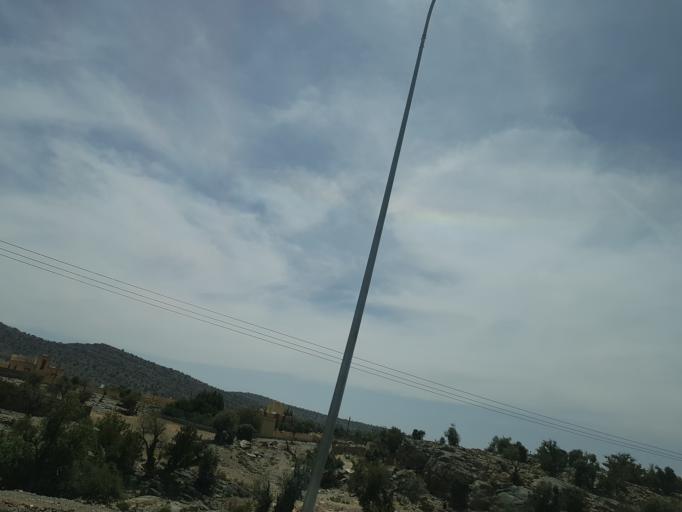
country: OM
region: Al Batinah
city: Bayt al `Awabi
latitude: 23.1387
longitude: 57.5744
